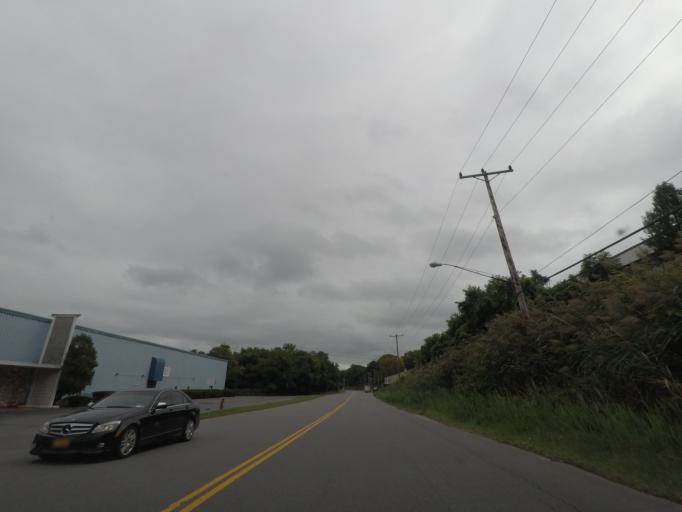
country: US
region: New York
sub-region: Albany County
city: West Albany
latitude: 42.6779
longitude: -73.7790
